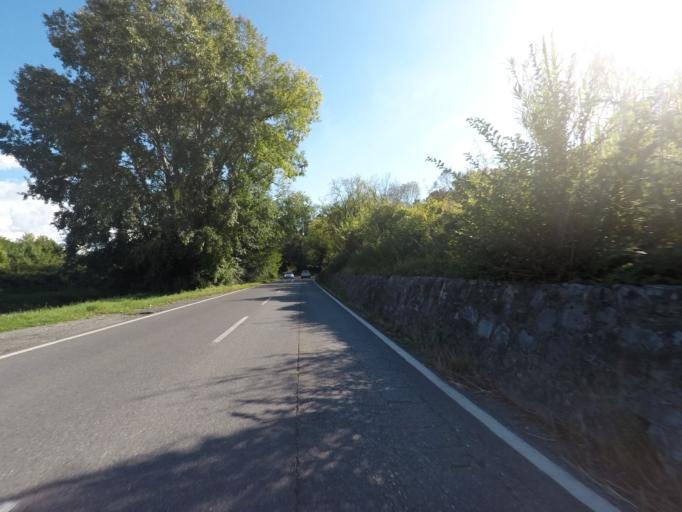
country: IT
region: Tuscany
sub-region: Provincia di Lucca
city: Lucca
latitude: 43.8738
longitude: 10.5206
